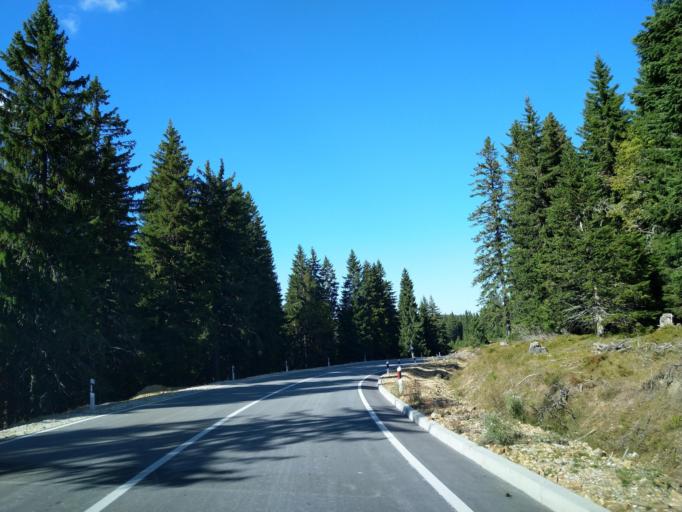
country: RS
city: Sokolovica
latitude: 43.3121
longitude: 20.2942
